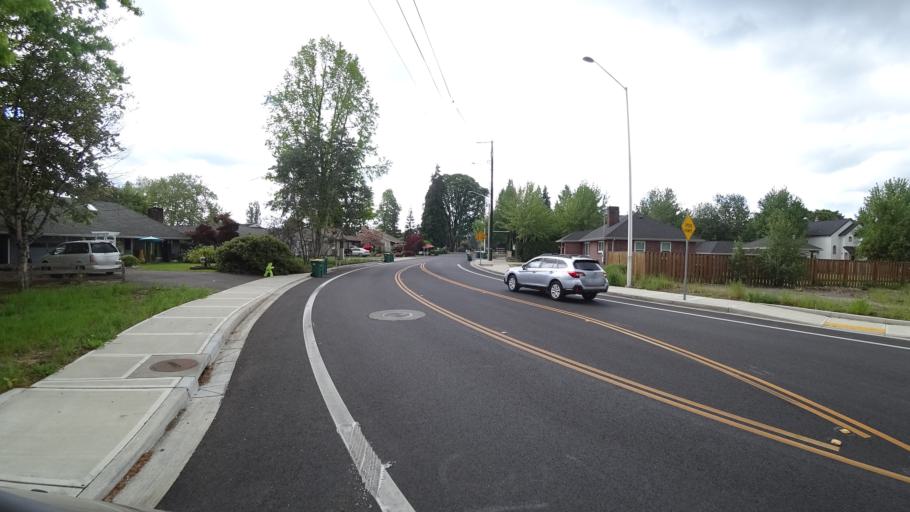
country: US
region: Oregon
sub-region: Washington County
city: Beaverton
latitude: 45.4858
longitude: -122.8218
